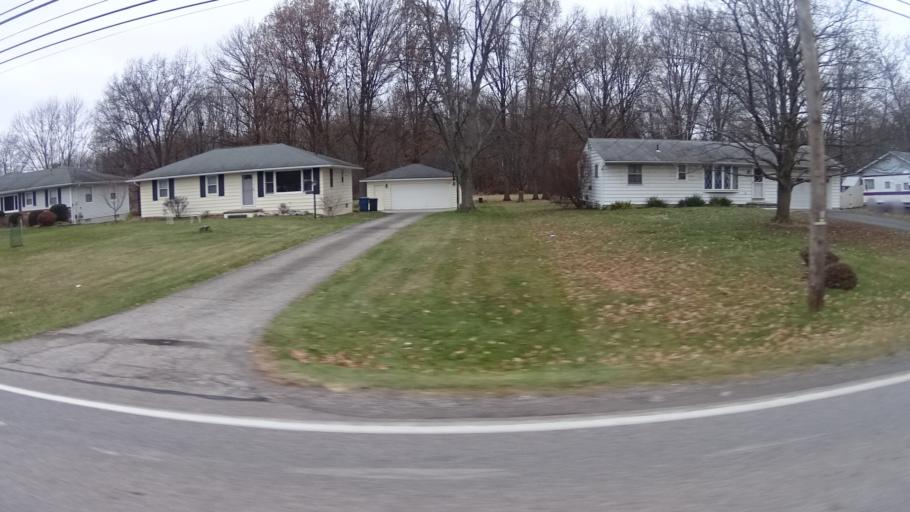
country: US
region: Ohio
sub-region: Lorain County
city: North Ridgeville
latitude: 41.3595
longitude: -82.0234
